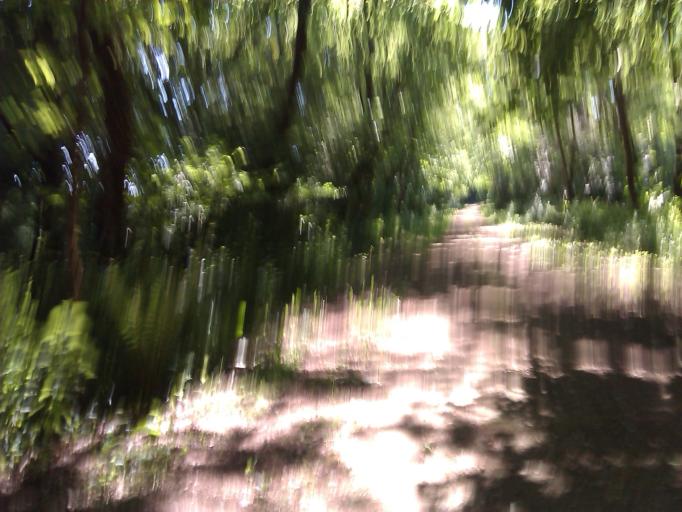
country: FR
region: Centre
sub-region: Departement de l'Indre
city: Saint-Gaultier
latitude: 46.6390
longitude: 1.3080
